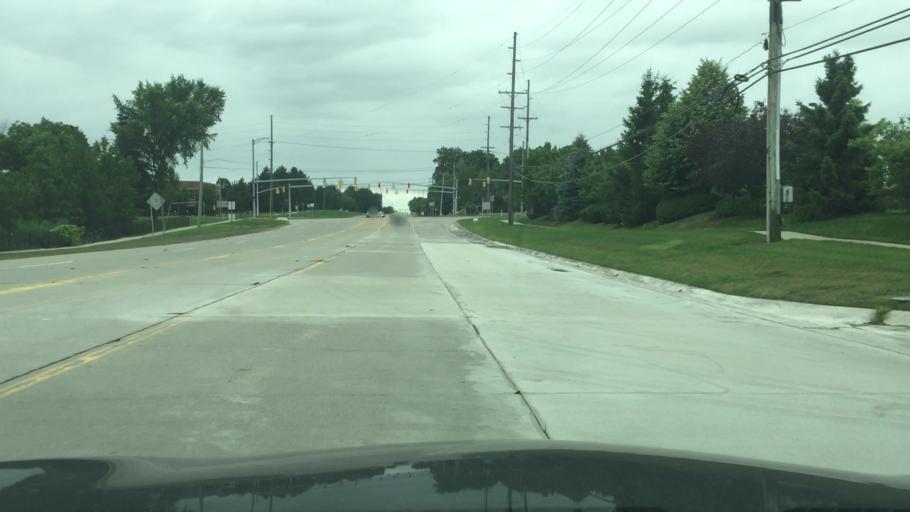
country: US
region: Michigan
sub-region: Oakland County
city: Novi
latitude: 42.4986
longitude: -83.4364
